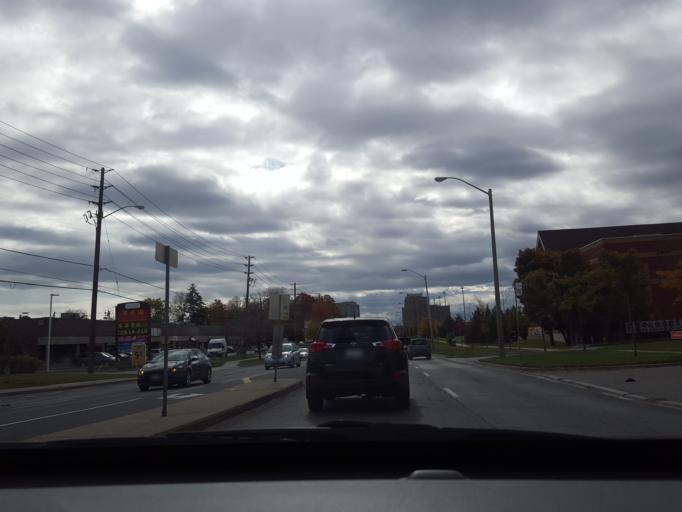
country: CA
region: Ontario
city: Markham
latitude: 43.8185
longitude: -79.3048
